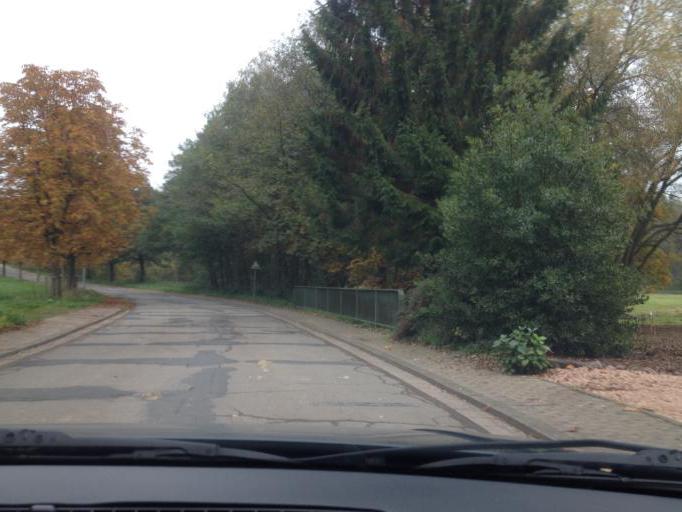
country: DE
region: Saarland
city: Eppelborn
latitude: 49.4472
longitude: 6.9685
